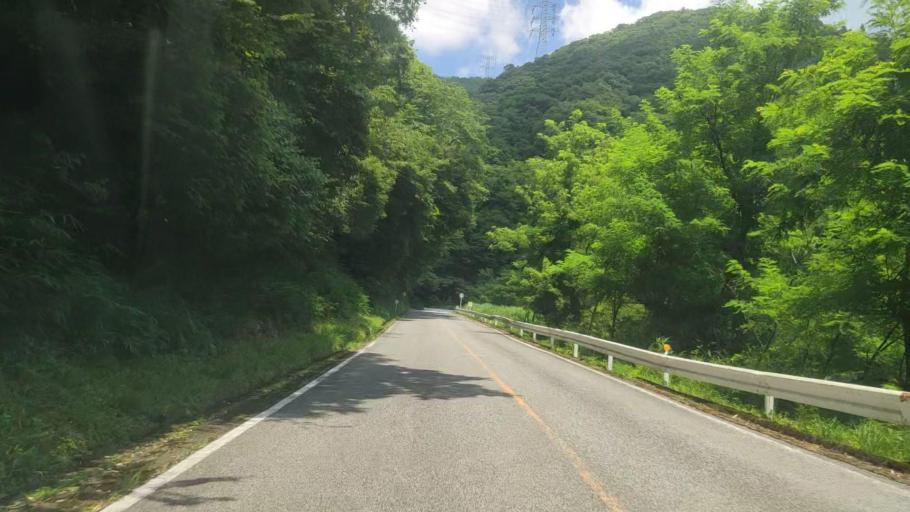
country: JP
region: Gifu
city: Tarui
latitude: 35.3799
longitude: 136.4440
